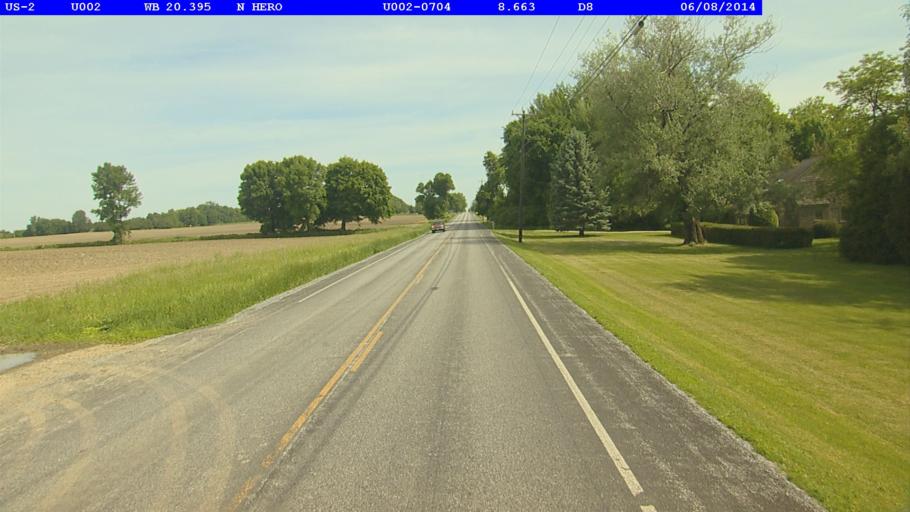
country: US
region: Vermont
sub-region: Grand Isle County
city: North Hero
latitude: 44.7751
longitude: -73.2939
